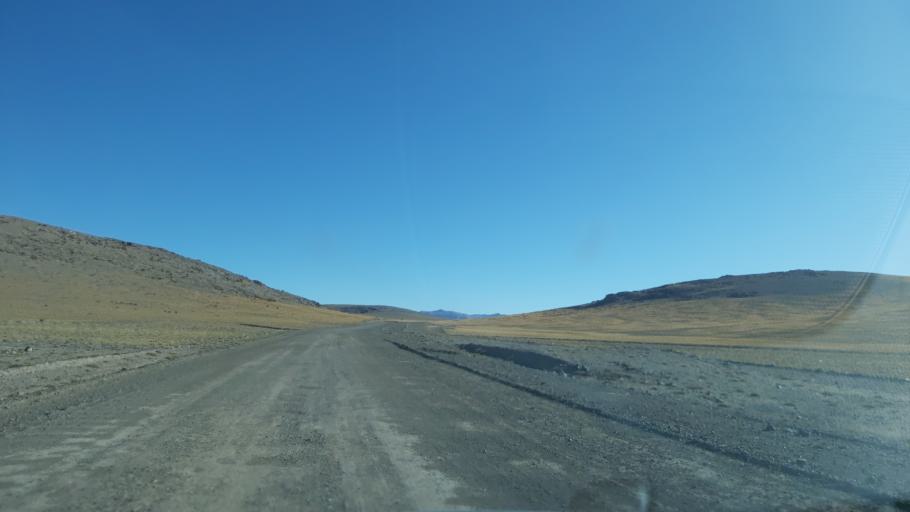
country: CL
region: Atacama
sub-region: Provincia de Chanaral
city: Diego de Almagro
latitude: -26.4613
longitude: -69.2925
